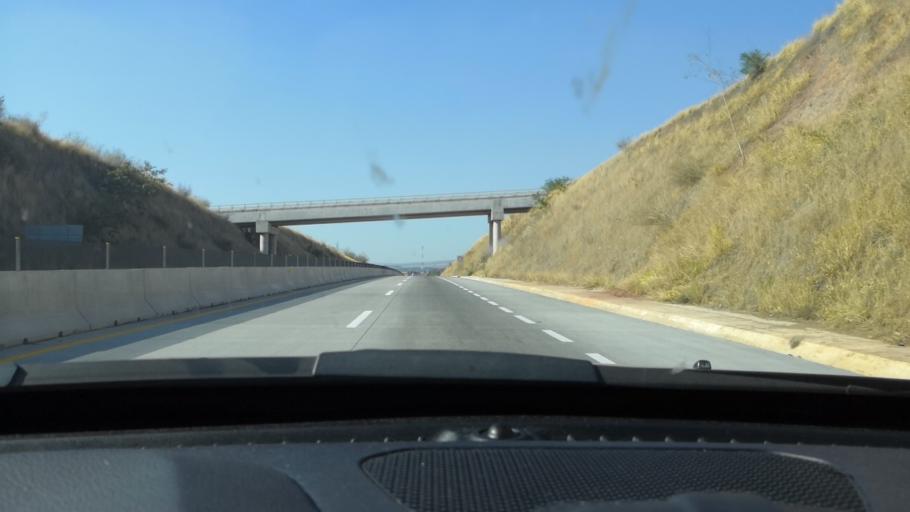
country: MX
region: Jalisco
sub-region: Zapotlanejo
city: La Mezquitera
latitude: 20.5918
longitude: -103.0996
